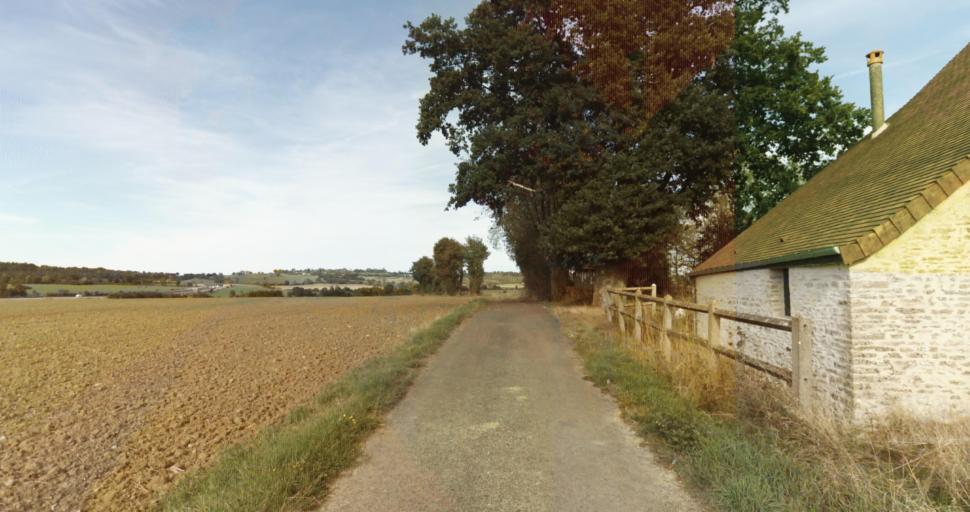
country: FR
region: Lower Normandy
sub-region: Departement de l'Orne
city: Gace
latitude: 48.7150
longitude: 0.2586
